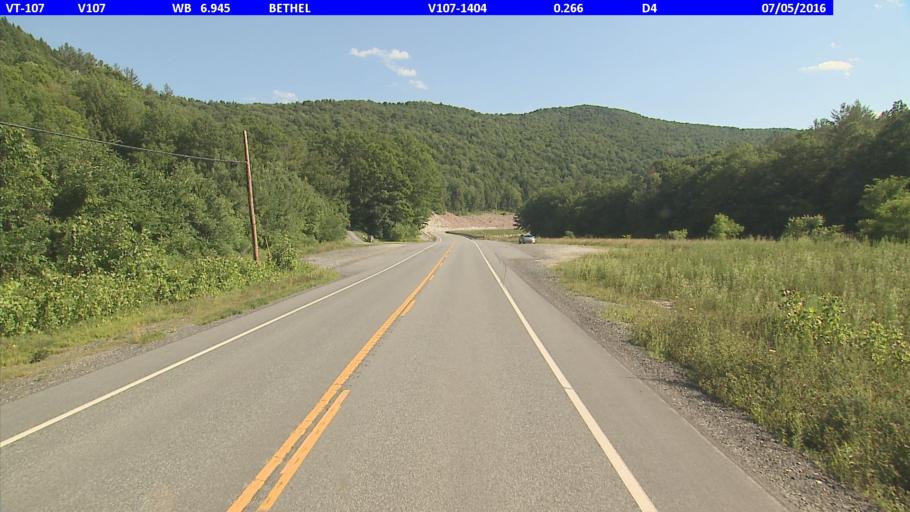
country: US
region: Vermont
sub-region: Orange County
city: Randolph
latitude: 43.7991
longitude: -72.6630
